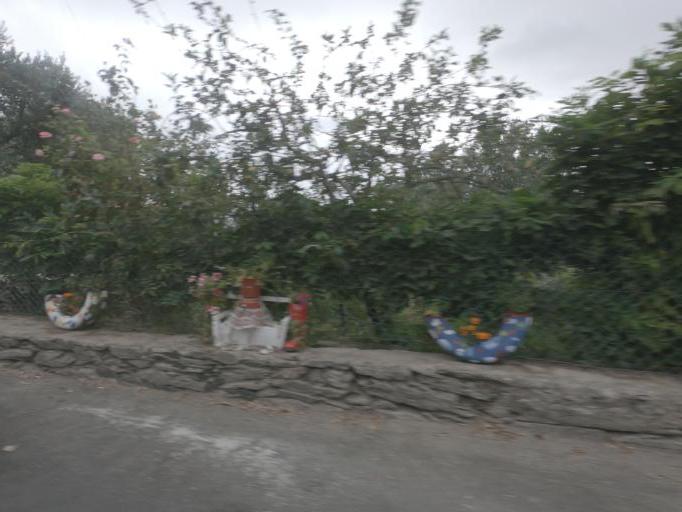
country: PT
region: Vila Real
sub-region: Sabrosa
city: Sabrosa
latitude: 41.2156
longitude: -7.5273
